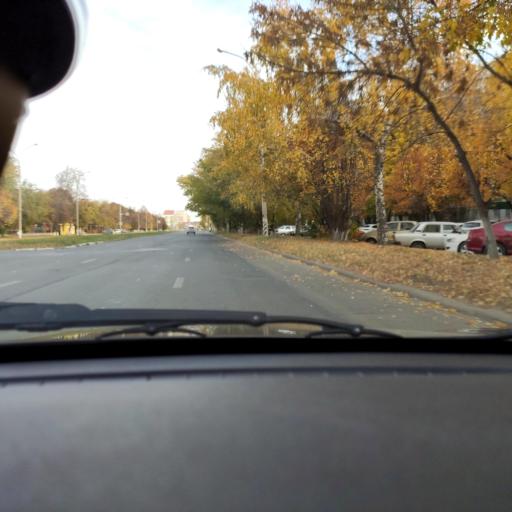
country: RU
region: Samara
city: Tol'yatti
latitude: 53.5160
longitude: 49.2645
